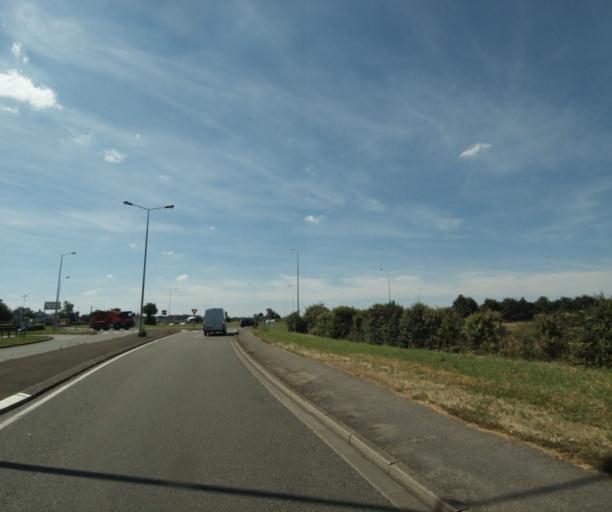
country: FR
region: Pays de la Loire
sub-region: Departement de la Mayenne
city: Change
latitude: 48.0802
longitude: -0.7944
